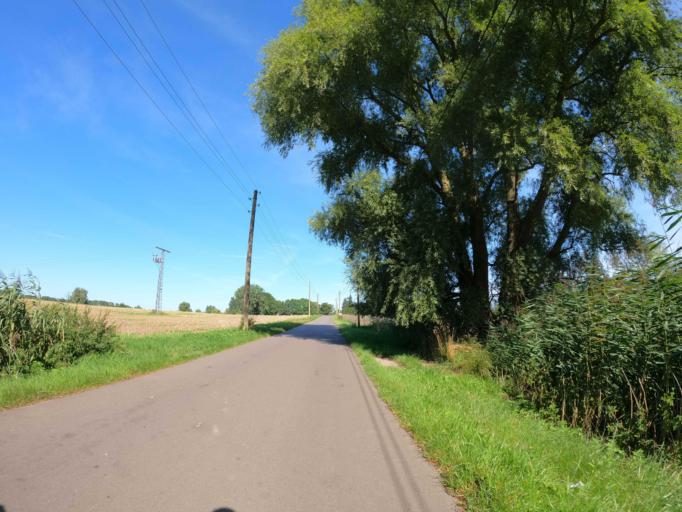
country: DE
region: Mecklenburg-Vorpommern
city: Kramerhof
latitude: 54.3707
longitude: 13.0489
